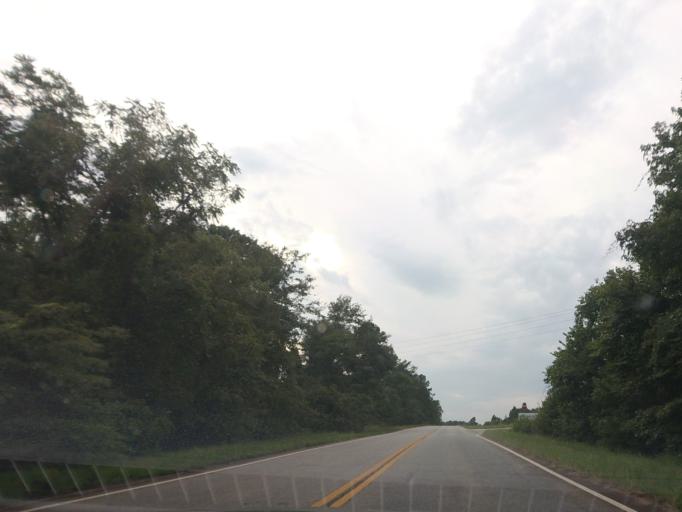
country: US
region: Georgia
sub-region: Twiggs County
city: Jeffersonville
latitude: 32.7170
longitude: -83.3946
